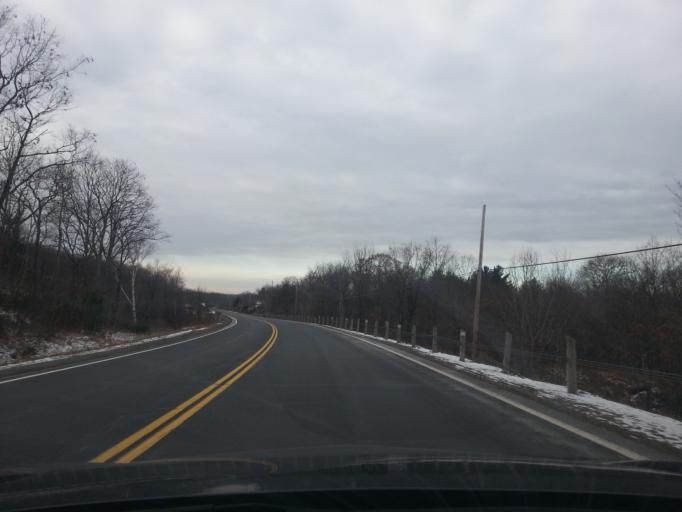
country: CA
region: Ontario
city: Greater Napanee
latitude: 44.6240
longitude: -77.1694
